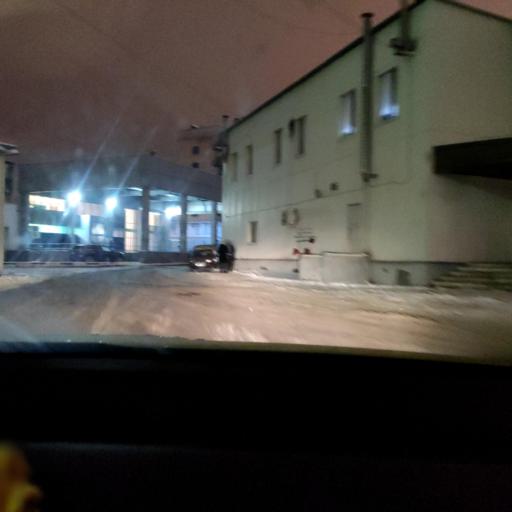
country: RU
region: Moscow
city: Rostokino
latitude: 55.8265
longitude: 37.6602
